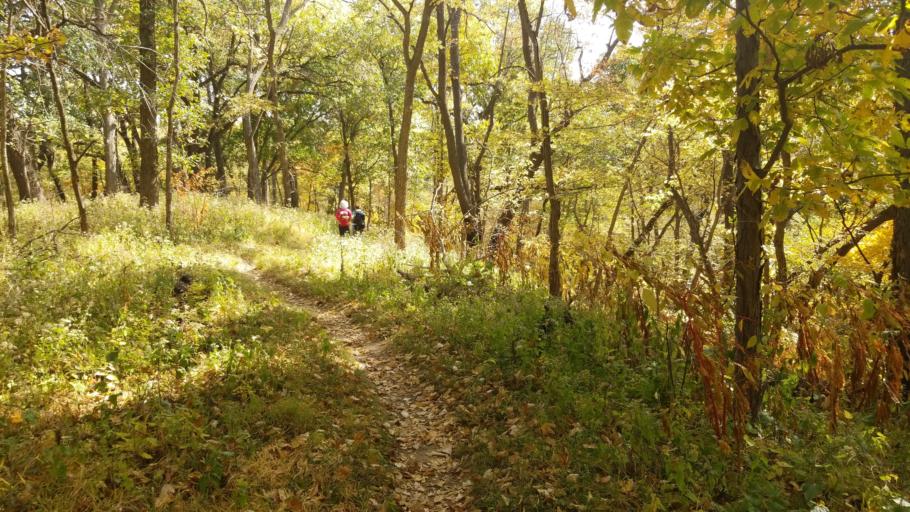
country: US
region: Nebraska
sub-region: Sarpy County
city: Bellevue
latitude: 41.1760
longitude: -95.8977
